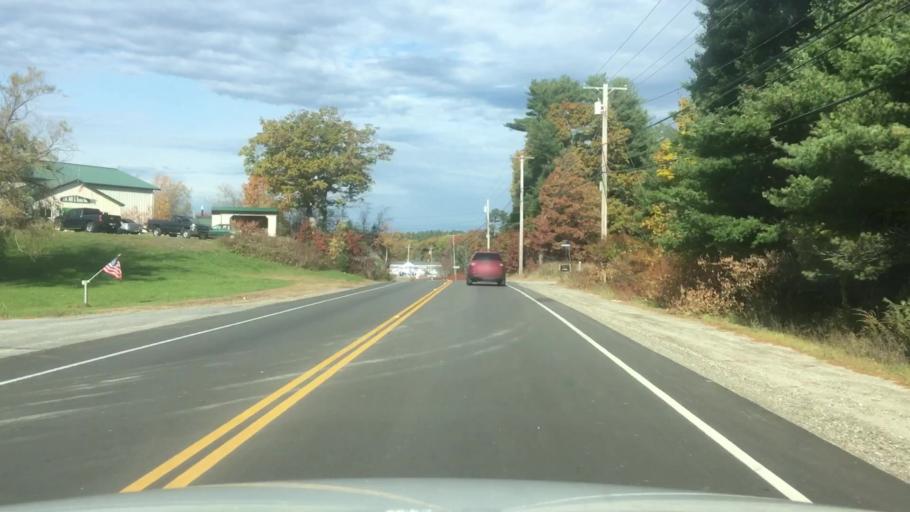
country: US
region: Maine
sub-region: Sagadahoc County
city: Bath
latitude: 43.9074
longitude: -69.8629
